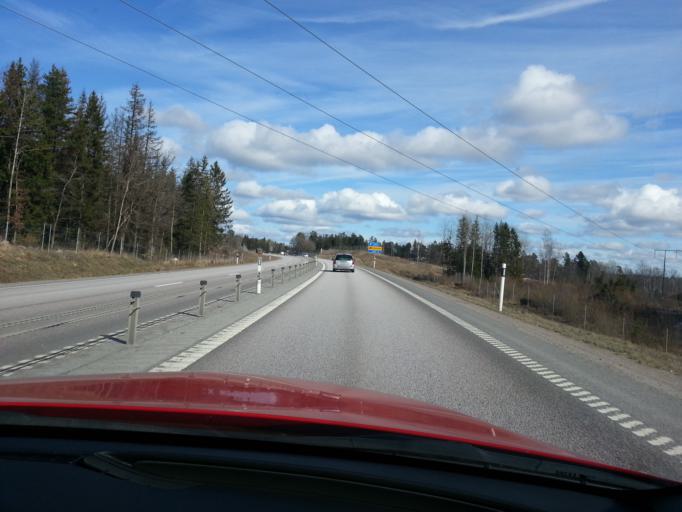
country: SE
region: Uppsala
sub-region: Uppsala Kommun
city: Storvreta
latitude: 59.9172
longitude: 17.7551
